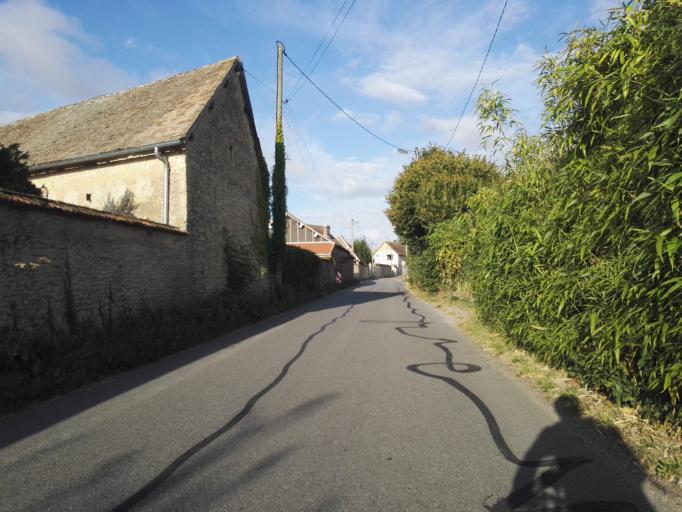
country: FR
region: Haute-Normandie
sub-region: Departement de l'Eure
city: Menilles
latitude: 49.0415
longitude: 1.3235
